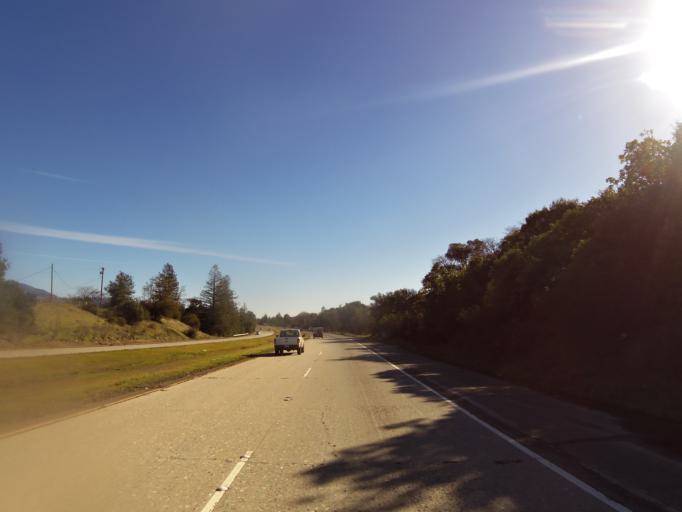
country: US
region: California
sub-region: Sonoma County
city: Cloverdale
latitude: 38.7630
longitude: -122.9872
